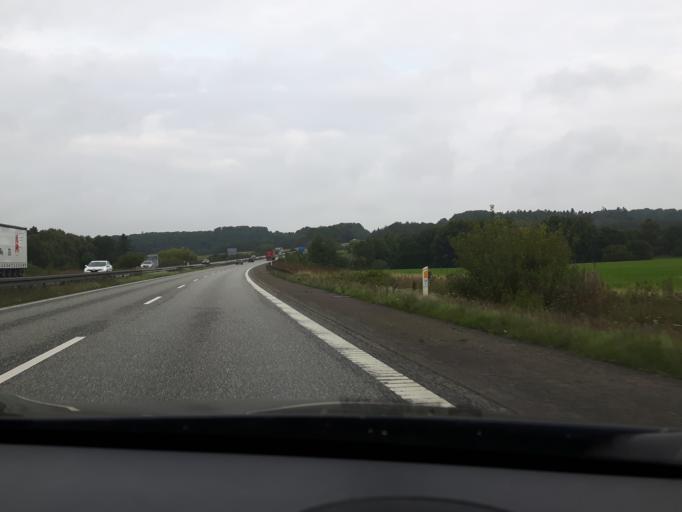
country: DK
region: North Denmark
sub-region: Mariagerfjord Kommune
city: Hobro
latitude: 56.6137
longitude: 9.7366
